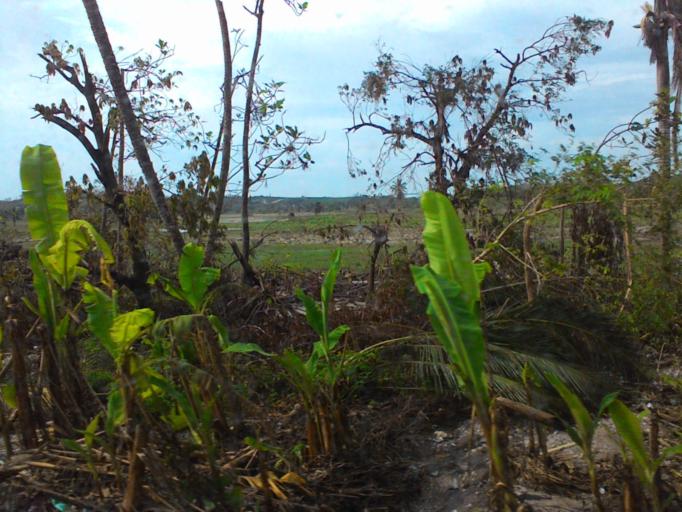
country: HT
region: Sud
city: Les Cayes
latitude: 18.2483
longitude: -73.7432
